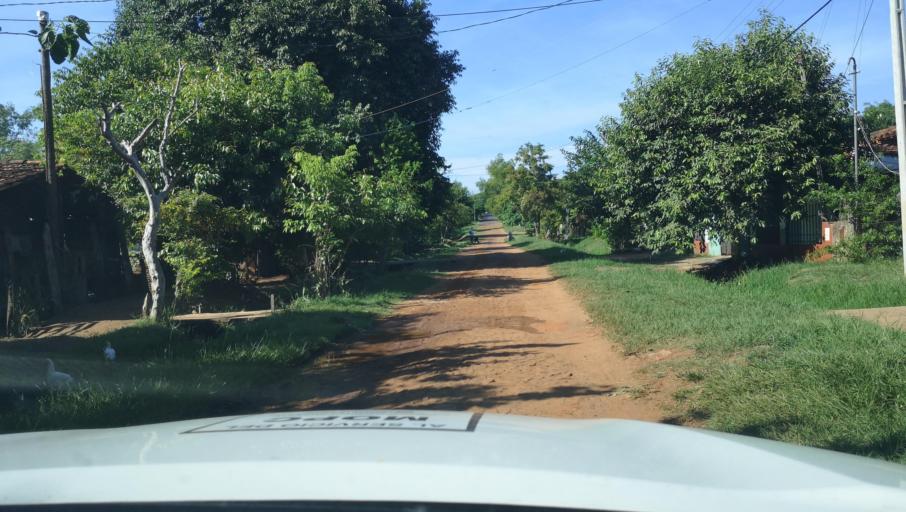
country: PY
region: Misiones
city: Santa Maria
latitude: -26.8838
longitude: -57.0163
